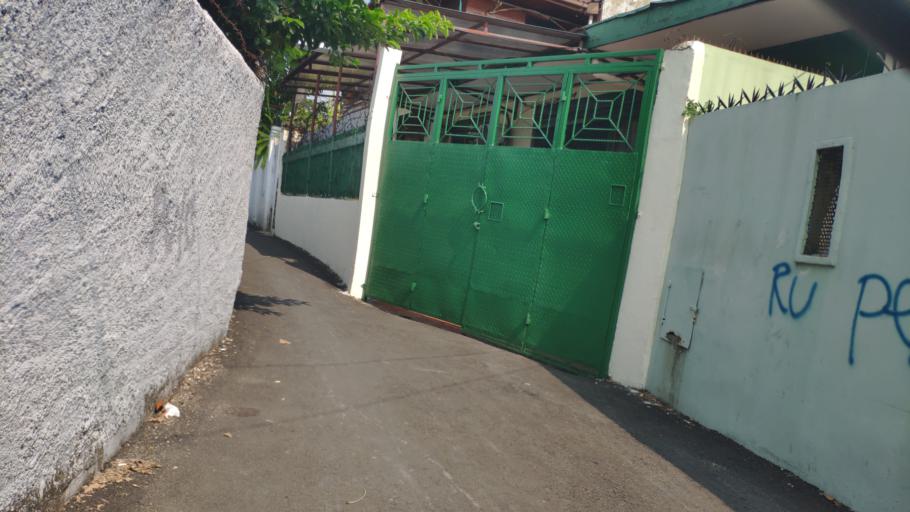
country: ID
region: Jakarta Raya
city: Jakarta
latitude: -6.2506
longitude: 106.7954
